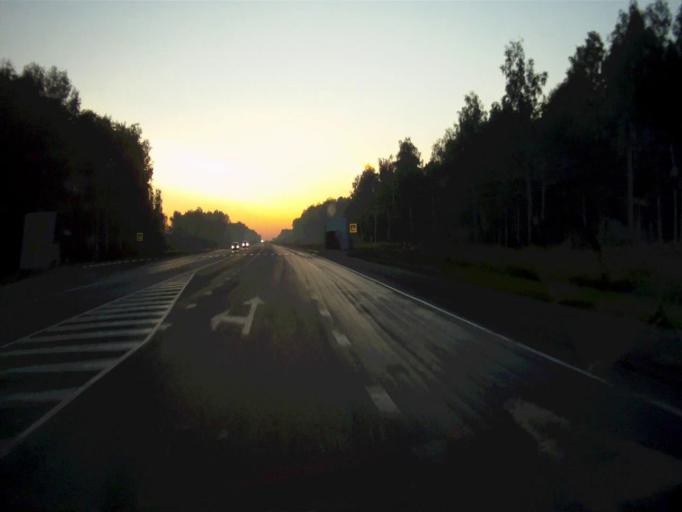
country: RU
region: Chelyabinsk
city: Poletayevo
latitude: 55.2066
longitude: 61.1045
